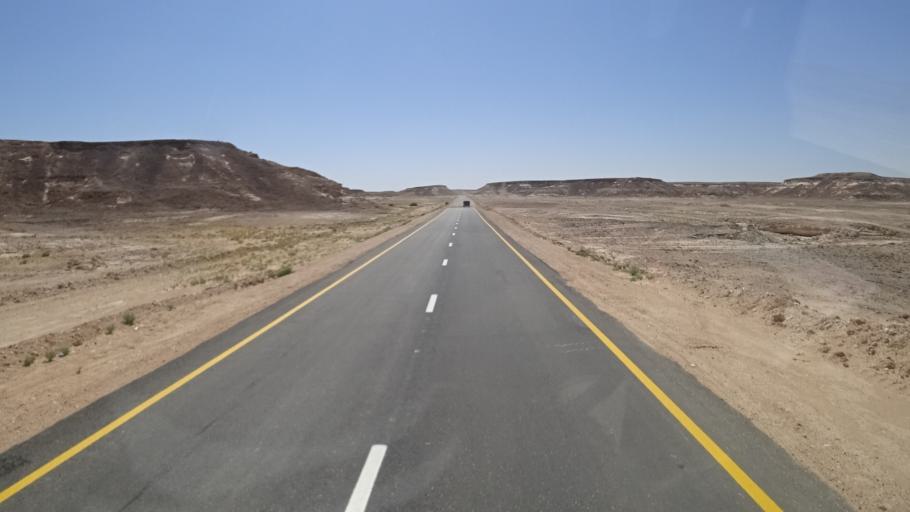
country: OM
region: Zufar
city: Salalah
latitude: 17.4743
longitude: 53.3481
